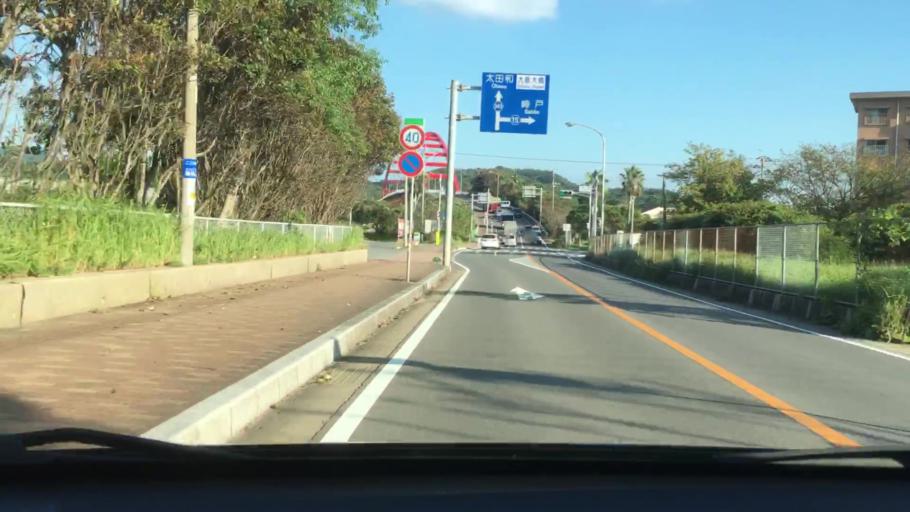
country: JP
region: Nagasaki
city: Sasebo
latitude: 33.0385
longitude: 129.6248
